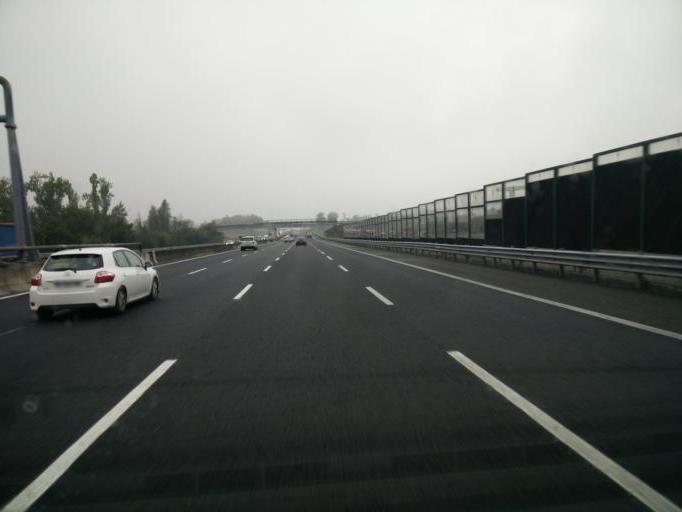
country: IT
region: Emilia-Romagna
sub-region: Provincia di Modena
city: San Damaso
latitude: 44.5827
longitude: 10.9689
